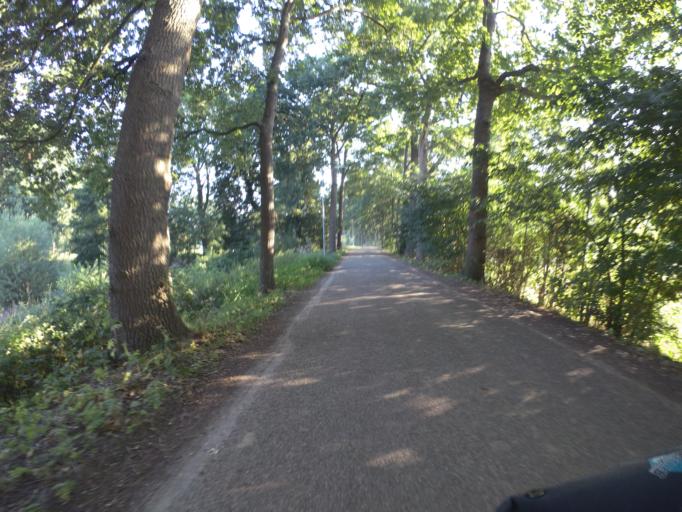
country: NL
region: North Brabant
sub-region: Gemeente Aalburg
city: Aalburg
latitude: 51.7504
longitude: 5.1496
